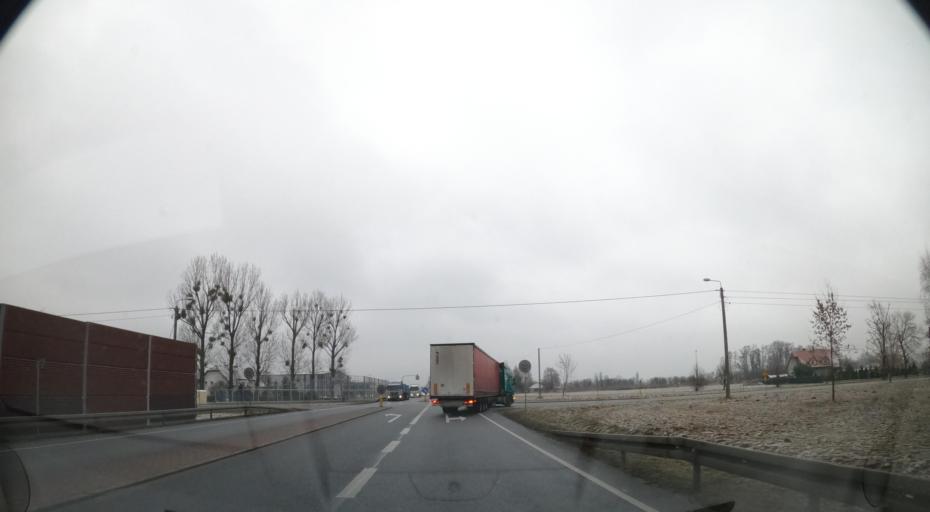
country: PL
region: Masovian Voivodeship
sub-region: Powiat sochaczewski
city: Sochaczew
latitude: 52.2386
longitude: 20.1826
